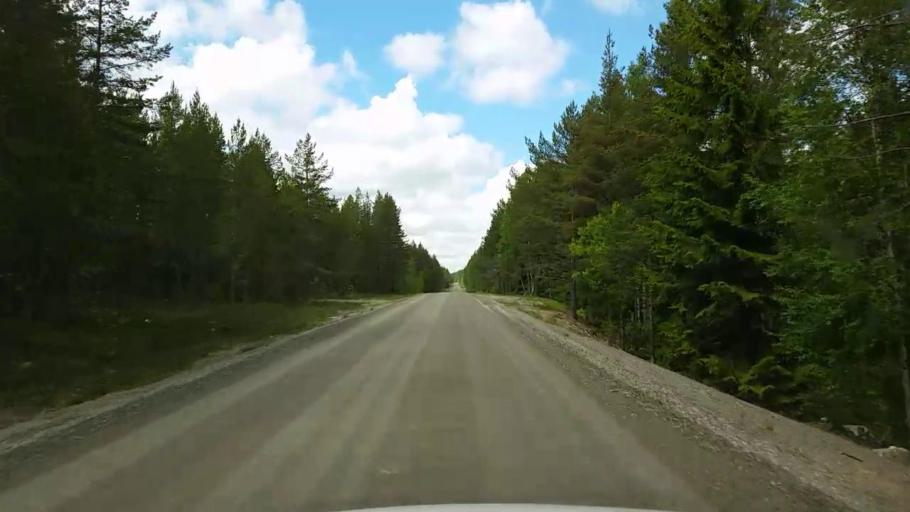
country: SE
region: Gaevleborg
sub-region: Bollnas Kommun
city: Kilafors
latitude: 61.0321
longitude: 16.3712
